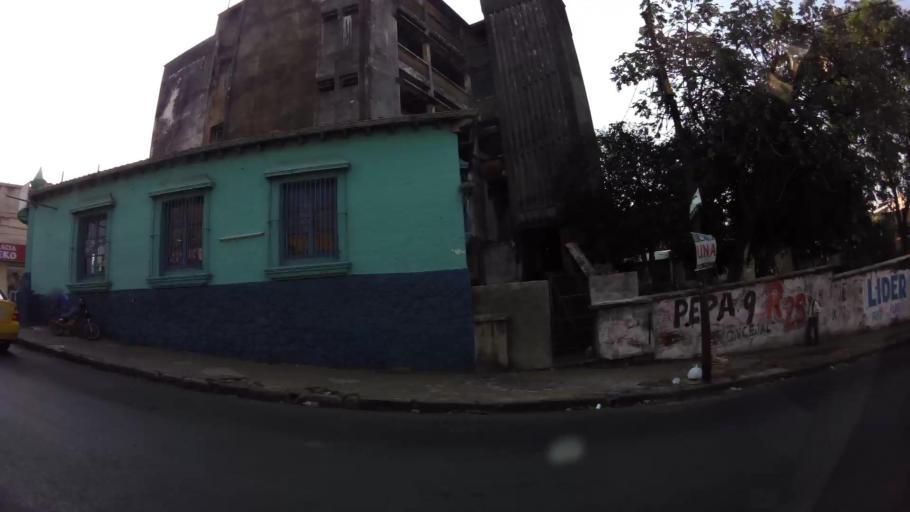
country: PY
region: Asuncion
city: Asuncion
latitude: -25.2955
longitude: -57.6237
